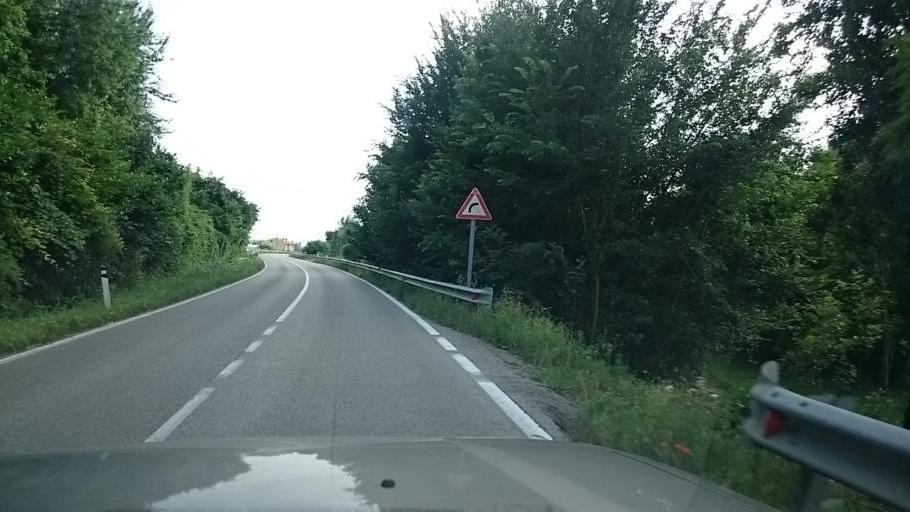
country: IT
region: Veneto
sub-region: Provincia di Padova
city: Santa Maria di Non
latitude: 45.5097
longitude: 11.8616
